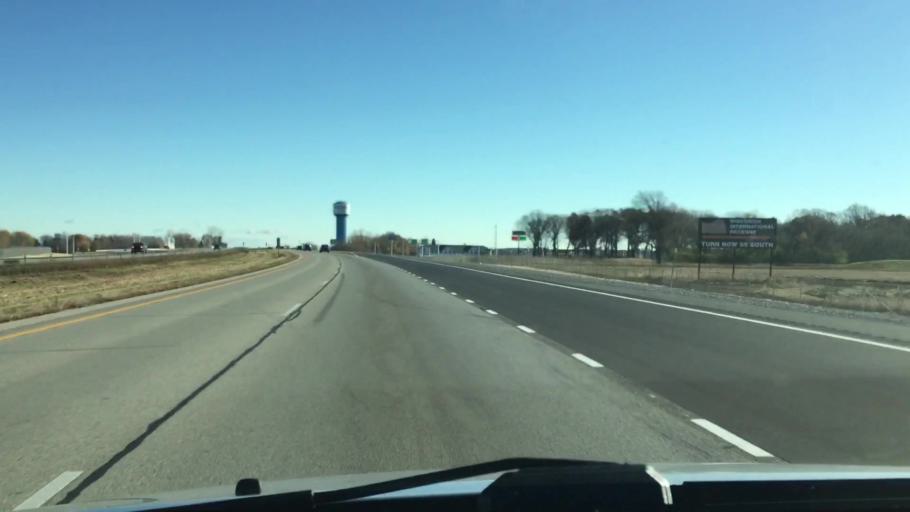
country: US
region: Wisconsin
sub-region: Outagamie County
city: Kaukauna
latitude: 44.2980
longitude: -88.2776
